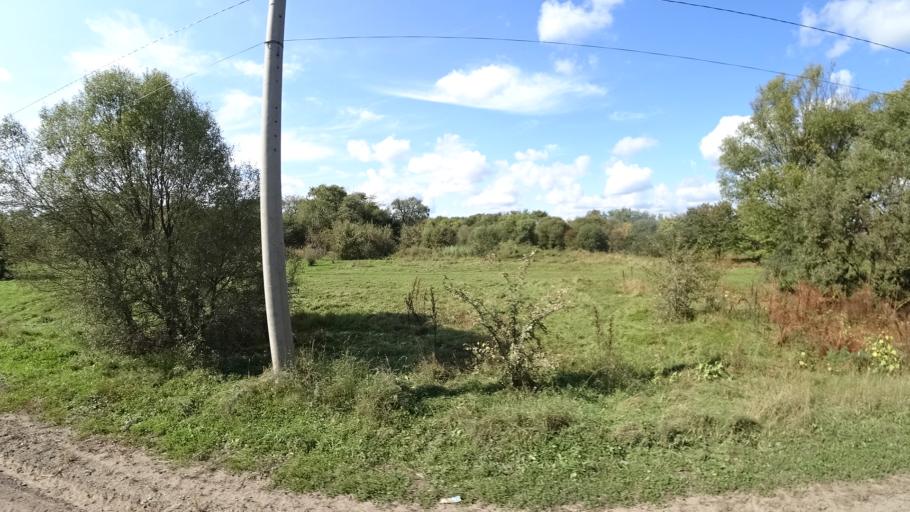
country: RU
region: Amur
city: Arkhara
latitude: 49.4025
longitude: 130.1515
